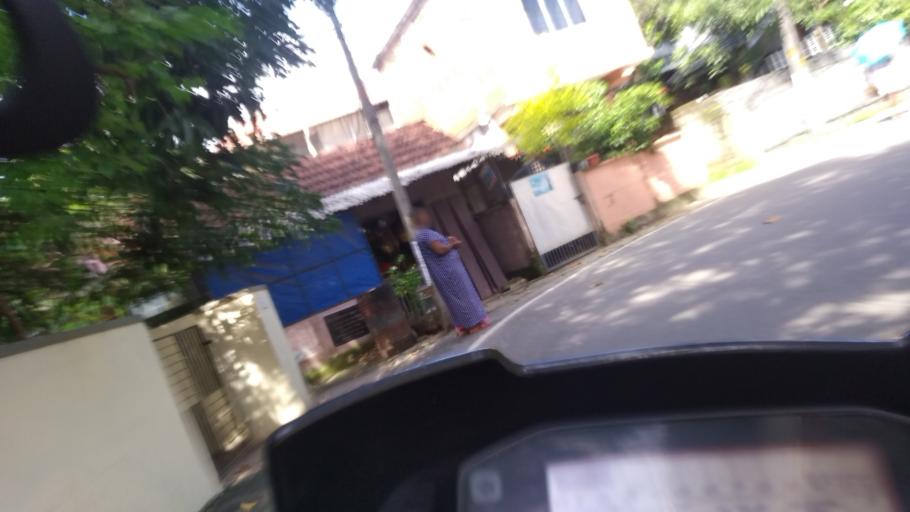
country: IN
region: Kerala
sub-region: Ernakulam
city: Elur
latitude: 10.0259
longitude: 76.2697
